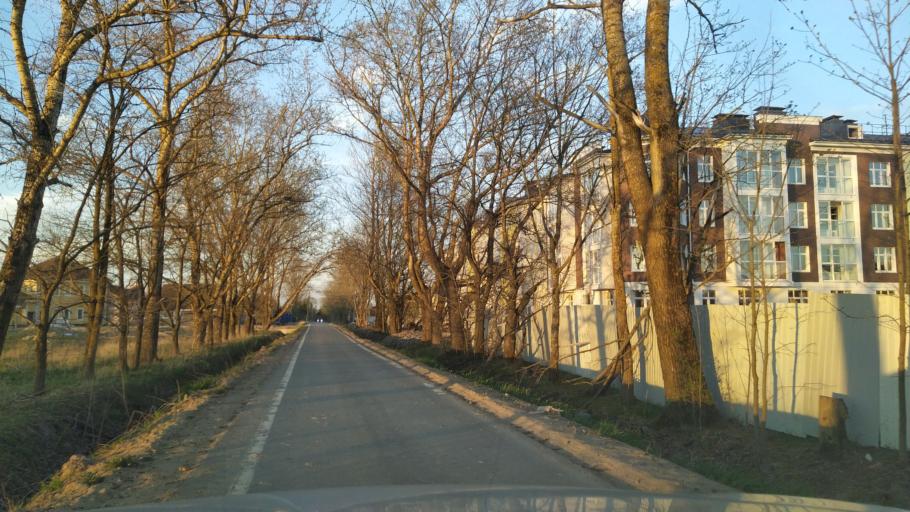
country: RU
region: St.-Petersburg
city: Pushkin
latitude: 59.6908
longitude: 30.4079
